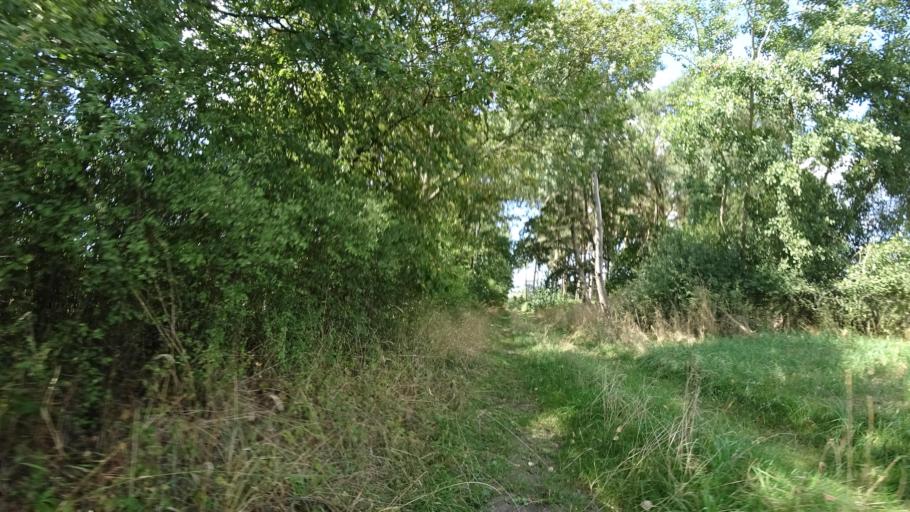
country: DE
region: North Rhine-Westphalia
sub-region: Regierungsbezirk Detmold
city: Rheda-Wiedenbruck
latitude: 51.8696
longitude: 8.2668
